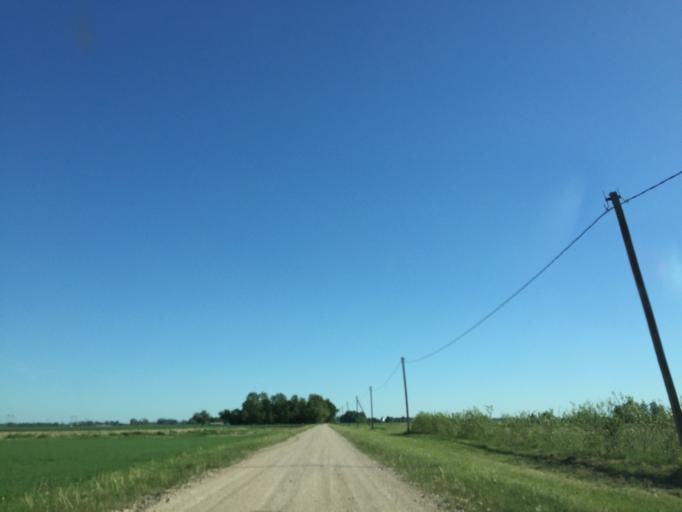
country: LV
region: Jelgava
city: Jelgava
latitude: 56.5405
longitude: 23.7182
